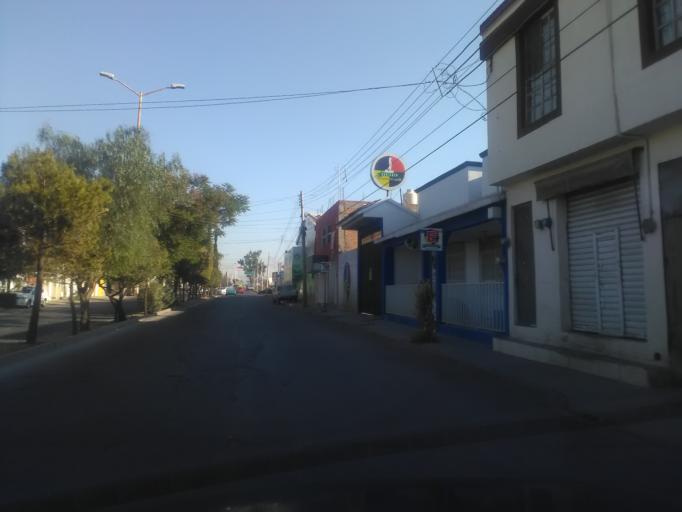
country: MX
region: Durango
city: Victoria de Durango
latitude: 24.0426
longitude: -104.6214
